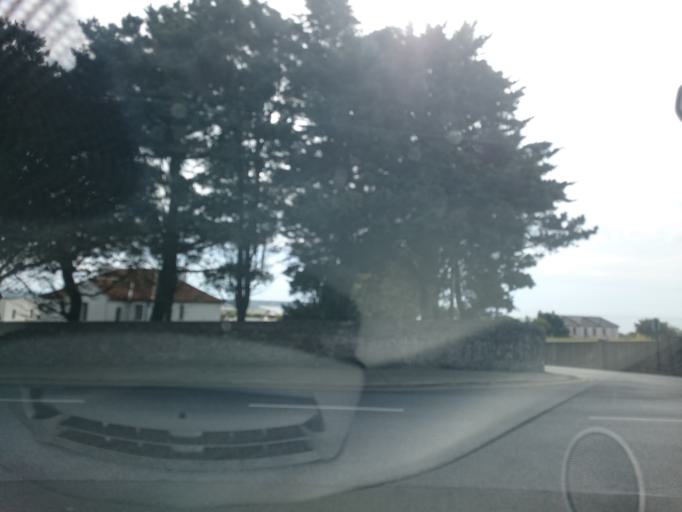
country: IE
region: Munster
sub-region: Waterford
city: Tra Mhor
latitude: 52.1658
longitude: -7.1523
